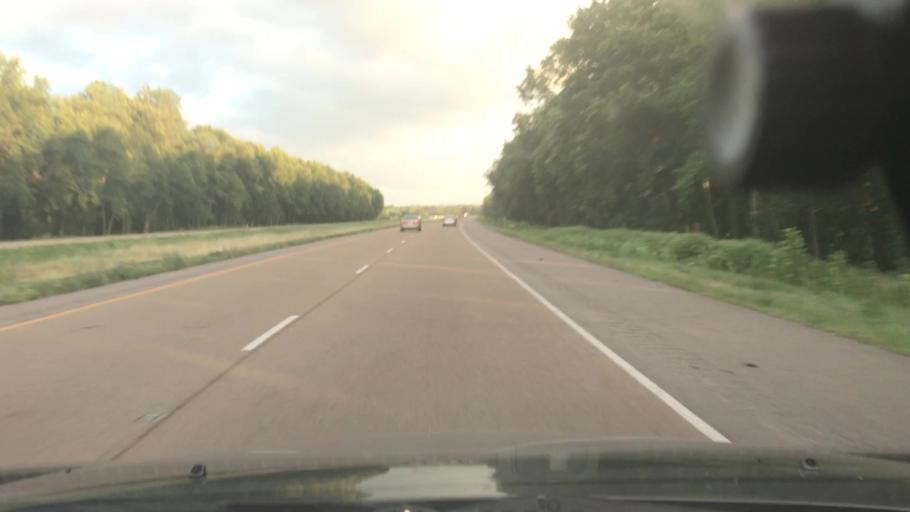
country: US
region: Illinois
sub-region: Washington County
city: Okawville
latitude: 38.4713
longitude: -89.5749
